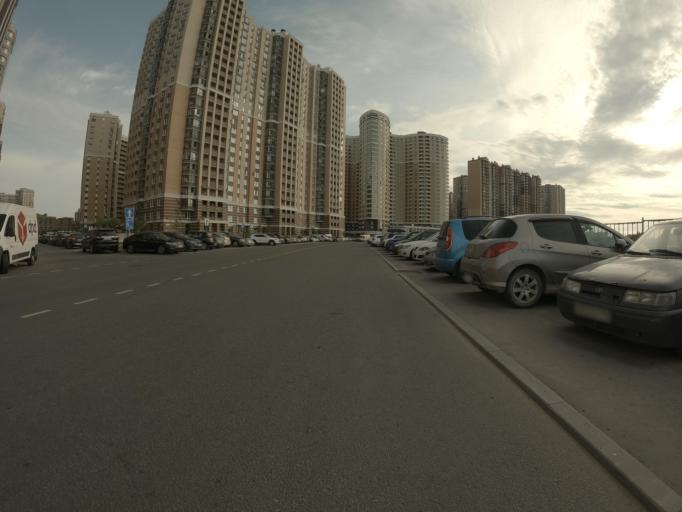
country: RU
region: St.-Petersburg
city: Krasnogvargeisky
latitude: 59.9193
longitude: 30.5152
